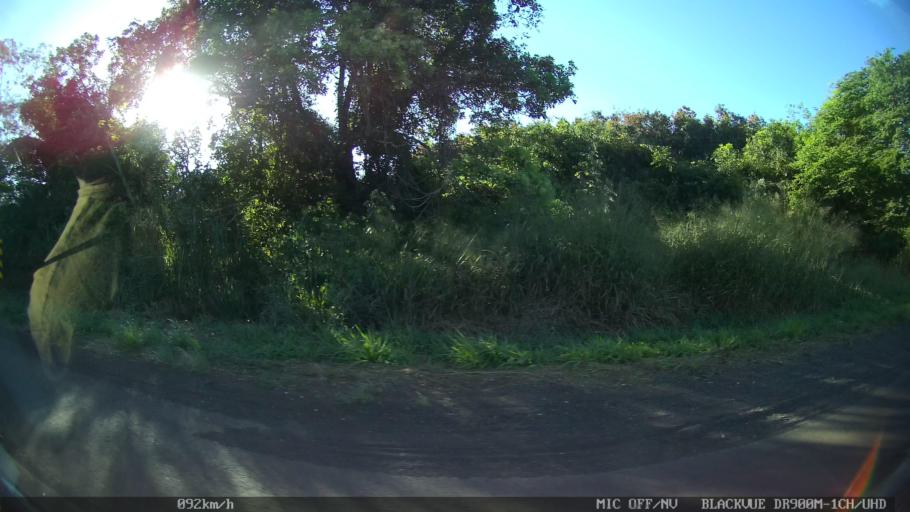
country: BR
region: Sao Paulo
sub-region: Guapiacu
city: Guapiacu
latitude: -20.7693
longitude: -49.2108
